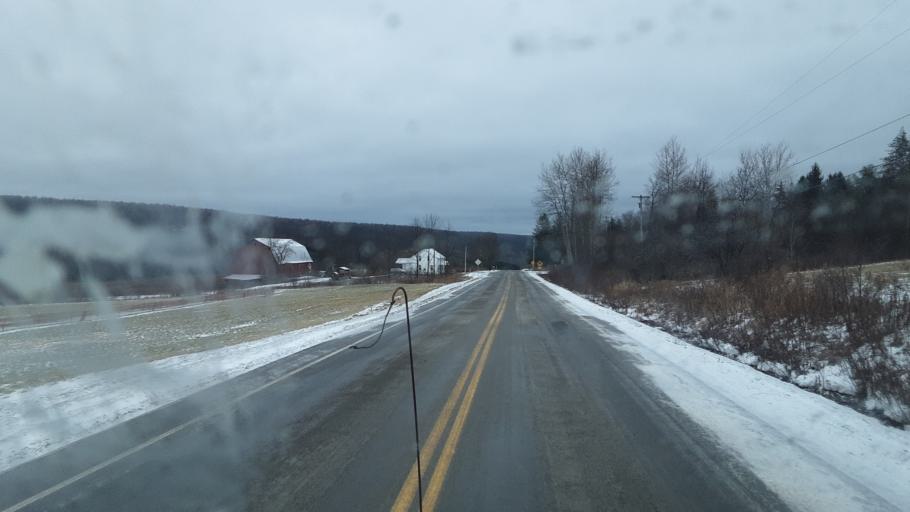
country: US
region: New York
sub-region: Allegany County
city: Friendship
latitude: 42.2477
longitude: -78.1475
